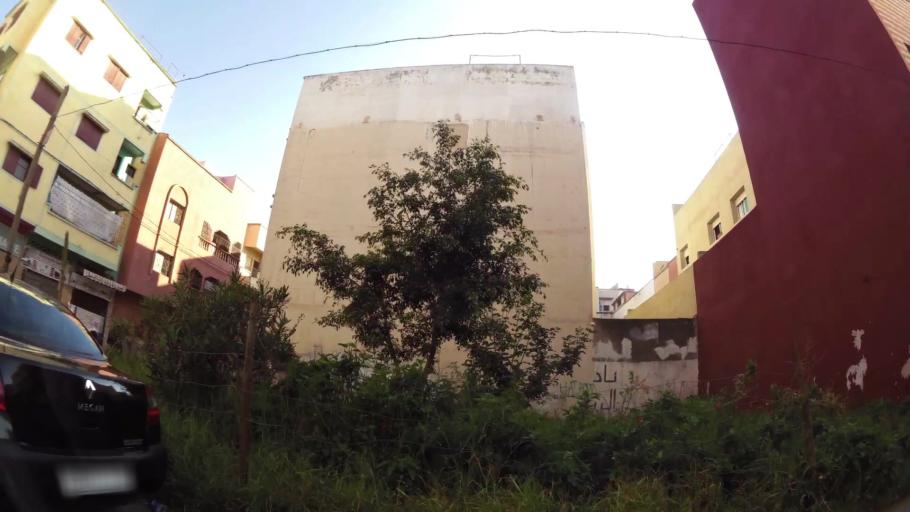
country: MA
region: Rabat-Sale-Zemmour-Zaer
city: Sale
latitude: 34.0541
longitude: -6.7918
